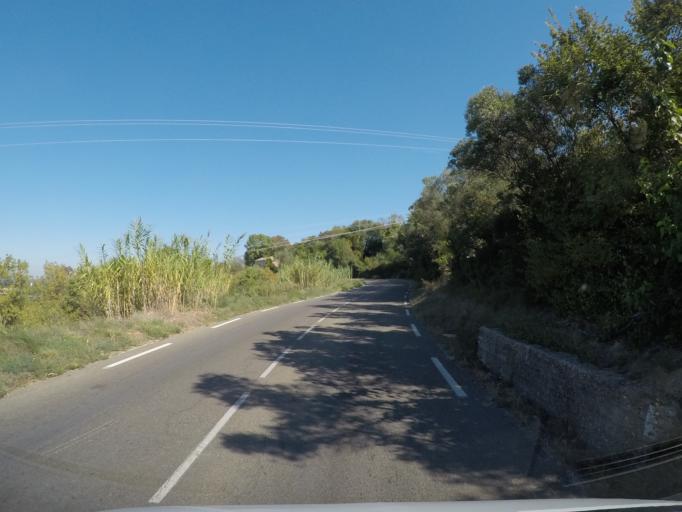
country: FR
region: Languedoc-Roussillon
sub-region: Departement du Gard
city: Uzes
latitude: 44.0061
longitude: 4.4045
